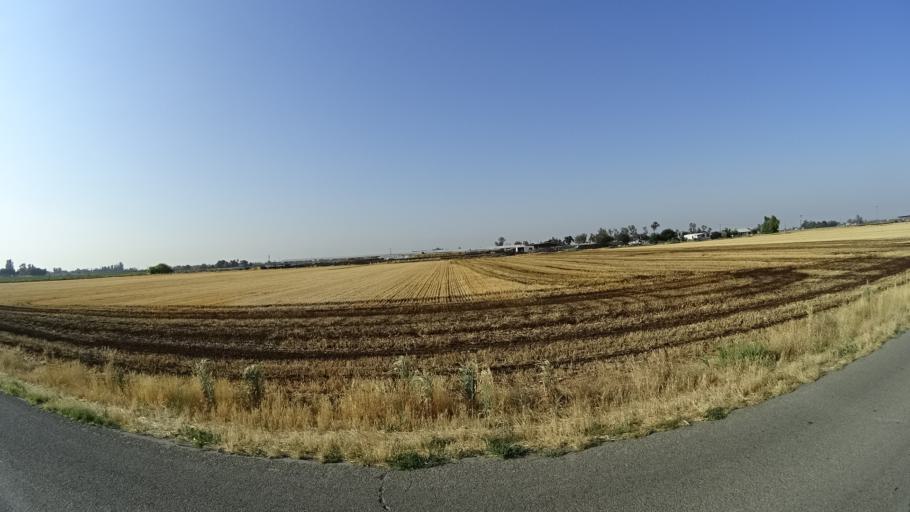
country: US
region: California
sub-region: Fresno County
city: Riverdale
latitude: 36.3803
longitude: -119.8405
